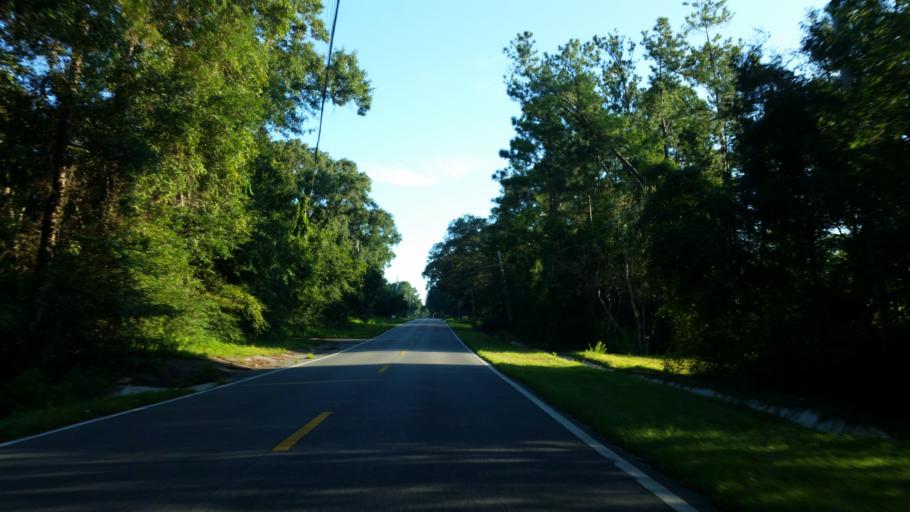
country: US
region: Florida
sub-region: Escambia County
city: Ensley
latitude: 30.5162
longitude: -87.3221
